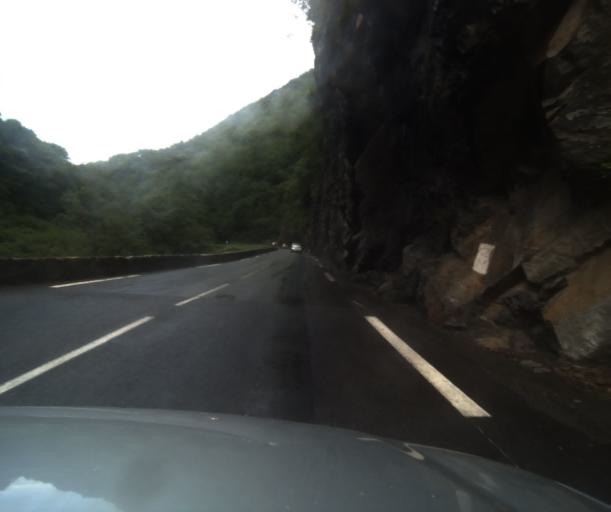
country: FR
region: Midi-Pyrenees
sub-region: Departement des Hautes-Pyrenees
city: Pierrefitte-Nestalas
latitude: 42.9351
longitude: -0.0487
